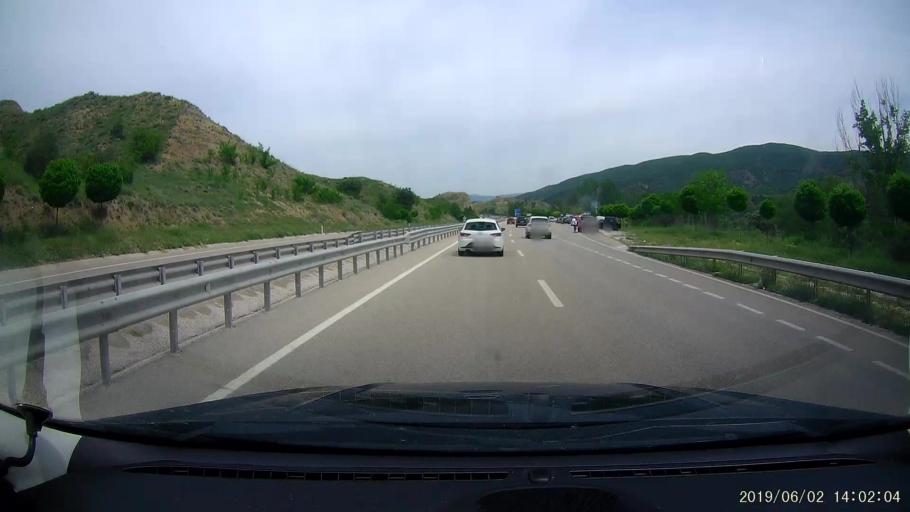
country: TR
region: Cankiri
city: Ilgaz
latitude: 40.9088
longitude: 33.6081
